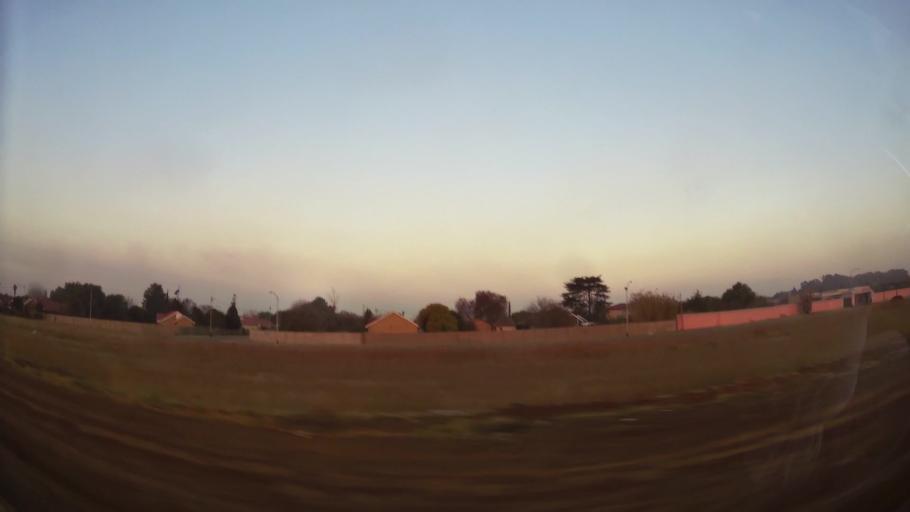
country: ZA
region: Gauteng
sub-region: Ekurhuleni Metropolitan Municipality
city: Springs
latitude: -26.3448
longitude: 28.4165
